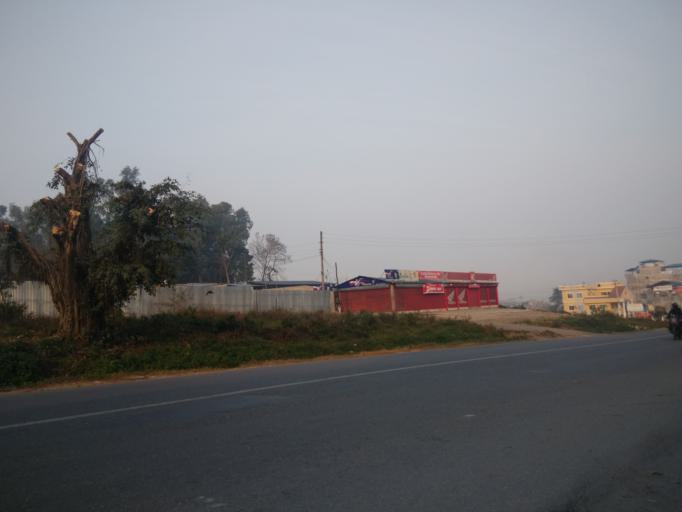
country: NP
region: Central Region
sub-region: Narayani Zone
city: Bharatpur
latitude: 27.6890
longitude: 84.4276
